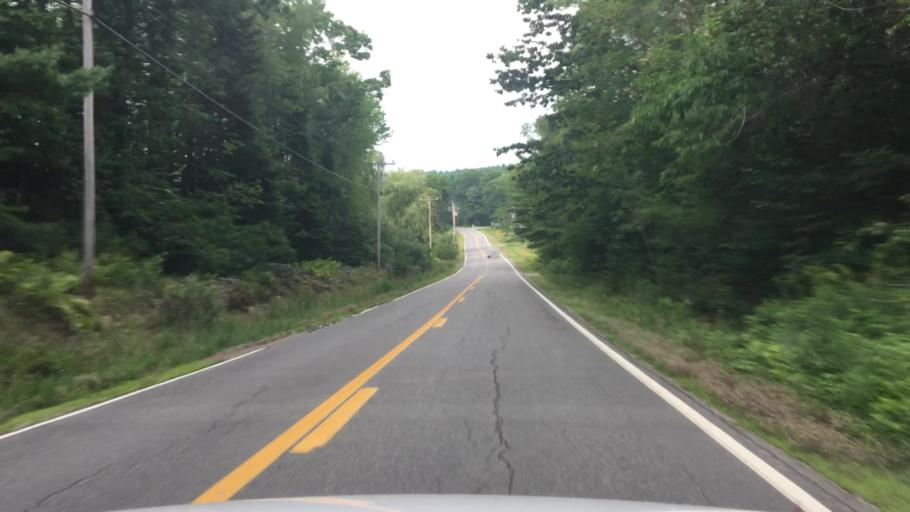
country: US
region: Maine
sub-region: Knox County
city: Washington
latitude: 44.2864
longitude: -69.3649
